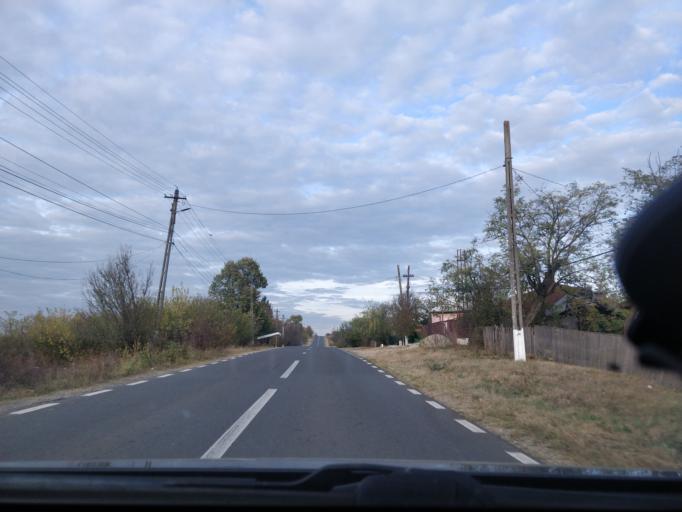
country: RO
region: Giurgiu
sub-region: Comuna Bucsani
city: Bucsani
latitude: 44.3789
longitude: 25.6556
